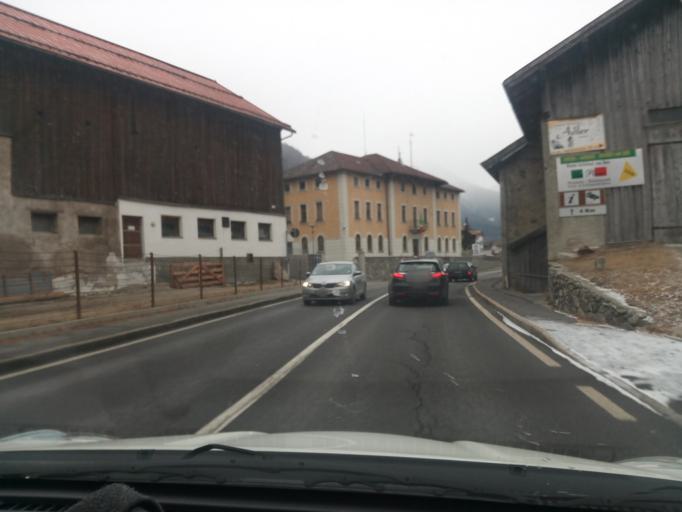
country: IT
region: Trentino-Alto Adige
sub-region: Bolzano
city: Curon Venosta
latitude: 46.8324
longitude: 10.5123
